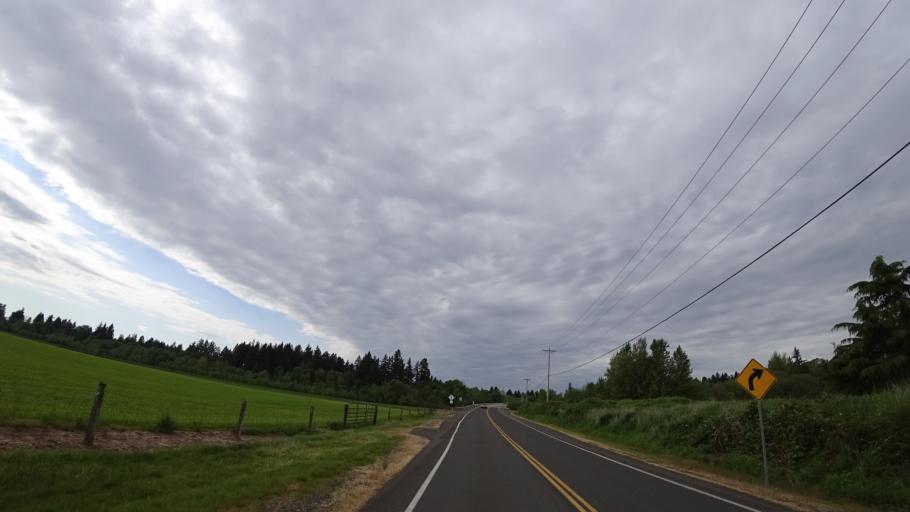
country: US
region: Oregon
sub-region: Washington County
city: Hillsboro
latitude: 45.4874
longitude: -122.9502
